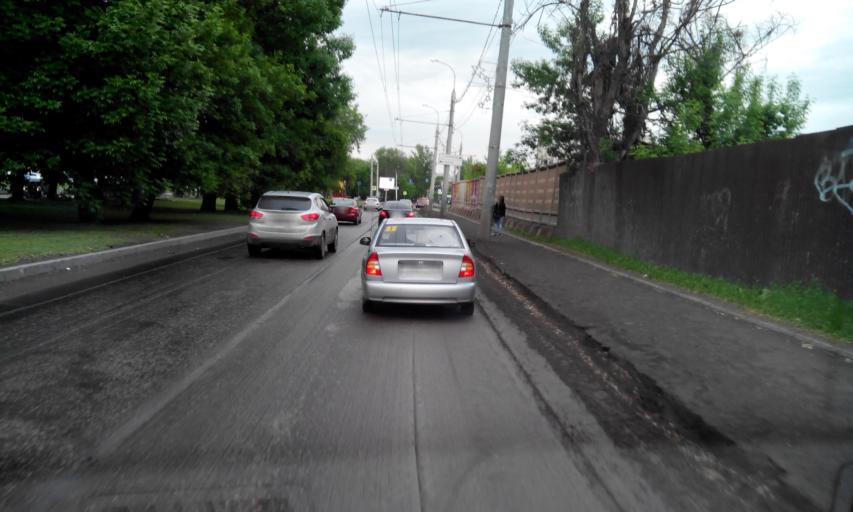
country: RU
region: Penza
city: Penza
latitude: 53.1961
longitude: 45.0068
